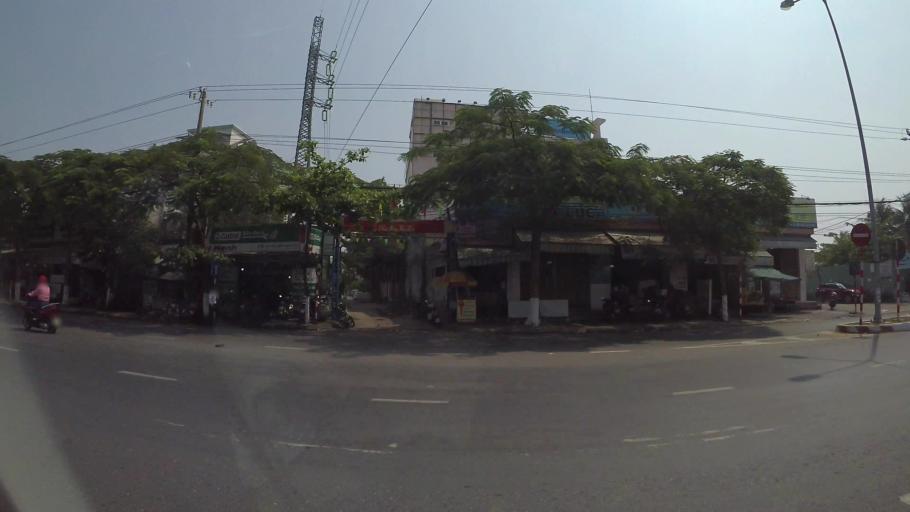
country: VN
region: Da Nang
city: Son Tra
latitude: 16.0525
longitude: 108.2371
